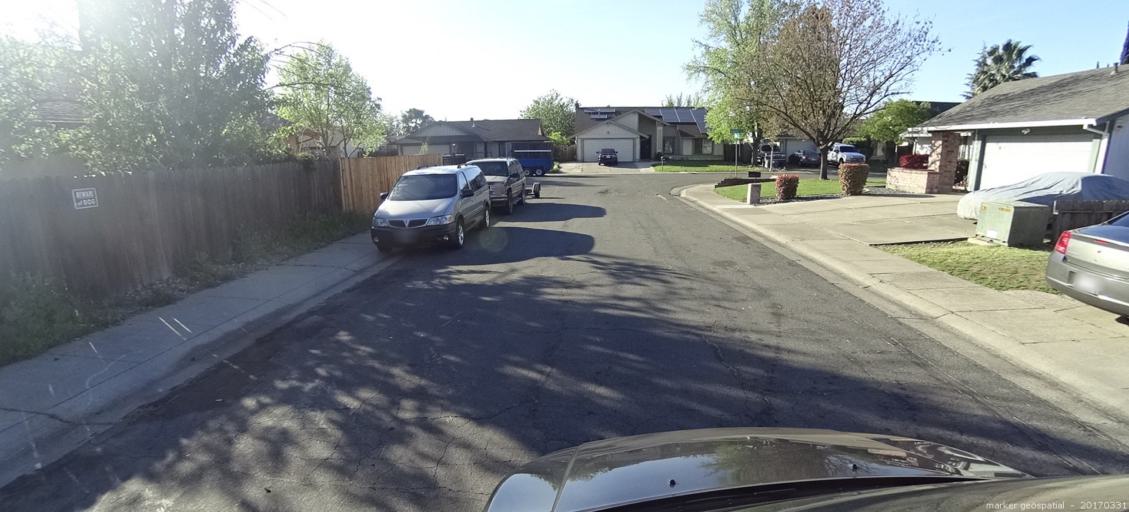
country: US
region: California
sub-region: Sacramento County
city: Parkway
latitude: 38.4688
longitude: -121.4512
